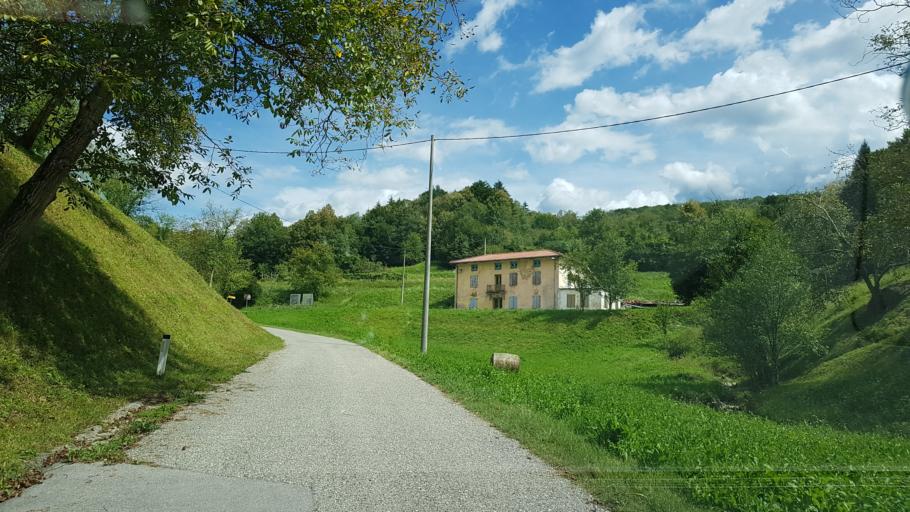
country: IT
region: Friuli Venezia Giulia
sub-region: Provincia di Udine
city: Stregna
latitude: 46.0990
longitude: 13.5856
